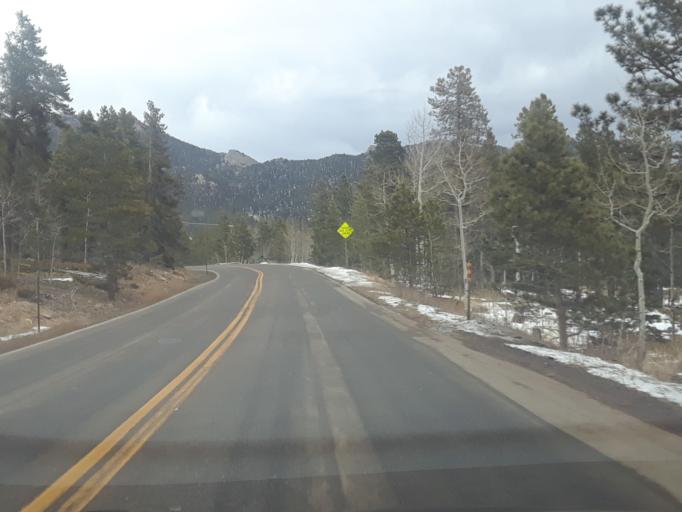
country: US
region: Colorado
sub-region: Gilpin County
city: Central City
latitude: 39.8398
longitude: -105.4605
